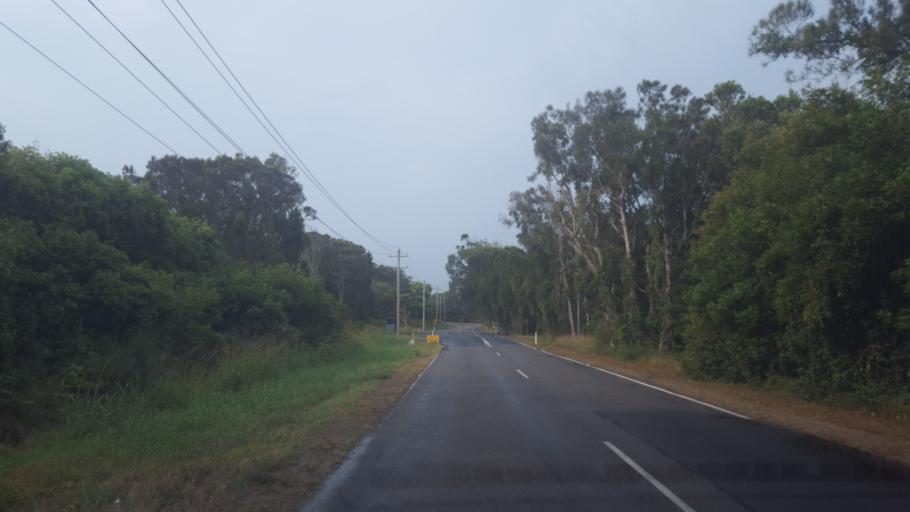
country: AU
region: New South Wales
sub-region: Port Stephens Shire
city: Anna Bay
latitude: -32.7721
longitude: 152.1146
